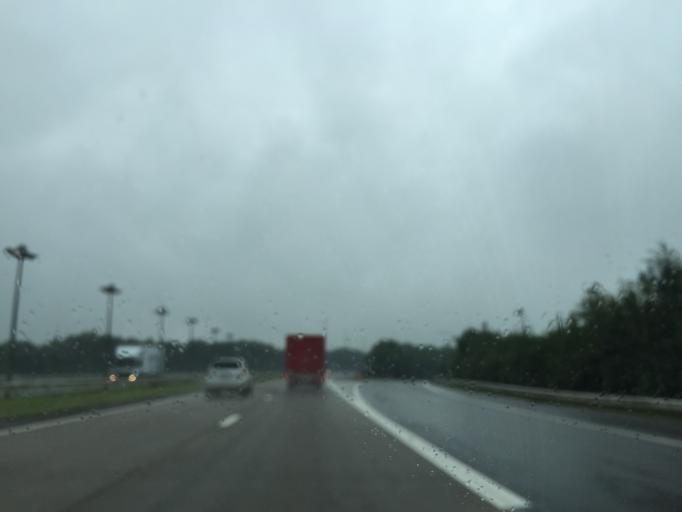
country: BE
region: Wallonia
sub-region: Province de Liege
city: Verviers
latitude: 50.5539
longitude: 5.8631
